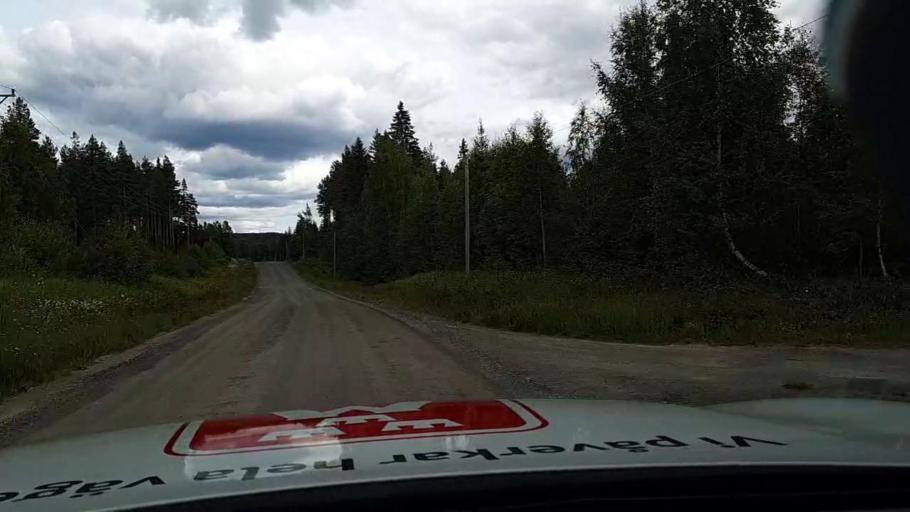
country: SE
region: Jaemtland
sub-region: Braecke Kommun
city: Braecke
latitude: 63.1921
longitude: 15.5160
